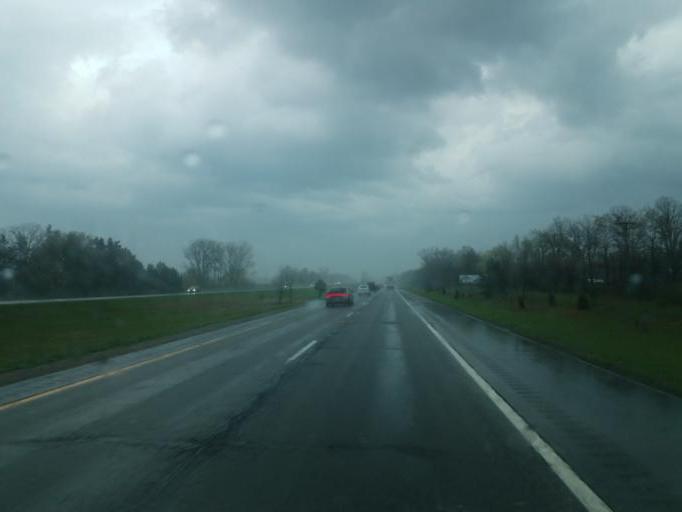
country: US
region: Michigan
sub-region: Ingham County
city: Webberville
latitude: 42.6512
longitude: -84.1630
